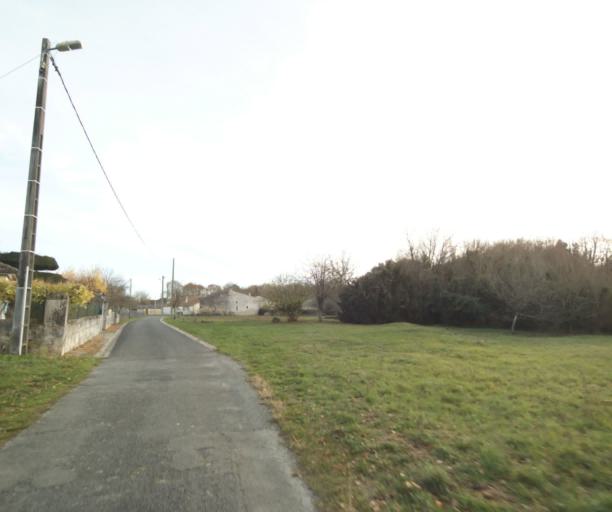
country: FR
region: Poitou-Charentes
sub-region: Departement de la Charente-Maritime
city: Saint-Hilaire-de-Villefranche
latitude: 45.8164
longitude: -0.5630
